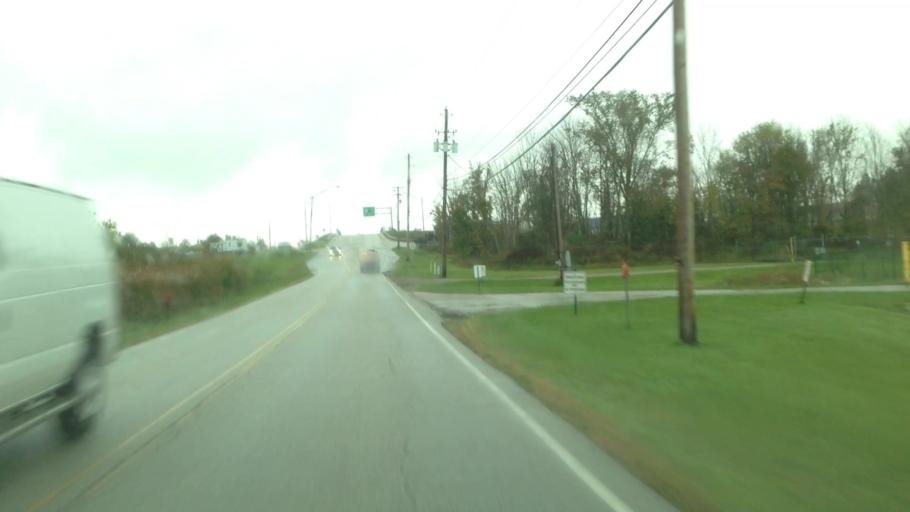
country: US
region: Ohio
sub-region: Summit County
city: Boston Heights
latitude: 41.2613
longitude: -81.4982
